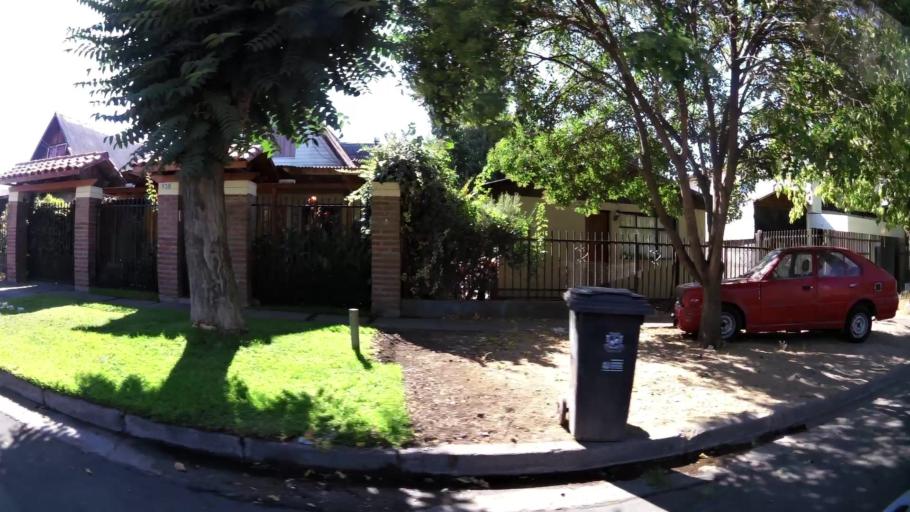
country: CL
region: Maule
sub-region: Provincia de Curico
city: Curico
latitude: -34.9821
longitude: -71.2537
